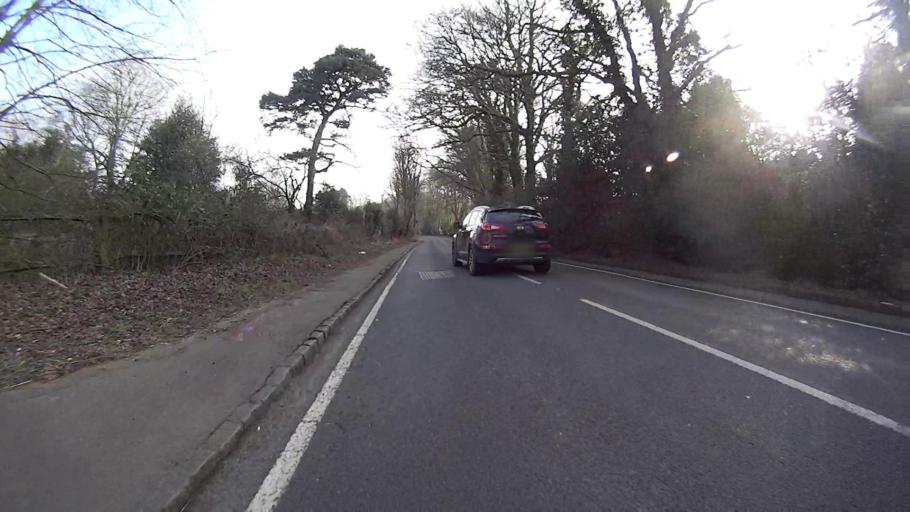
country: GB
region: England
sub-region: West Sussex
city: Crawley Down
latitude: 51.1334
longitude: -0.0923
